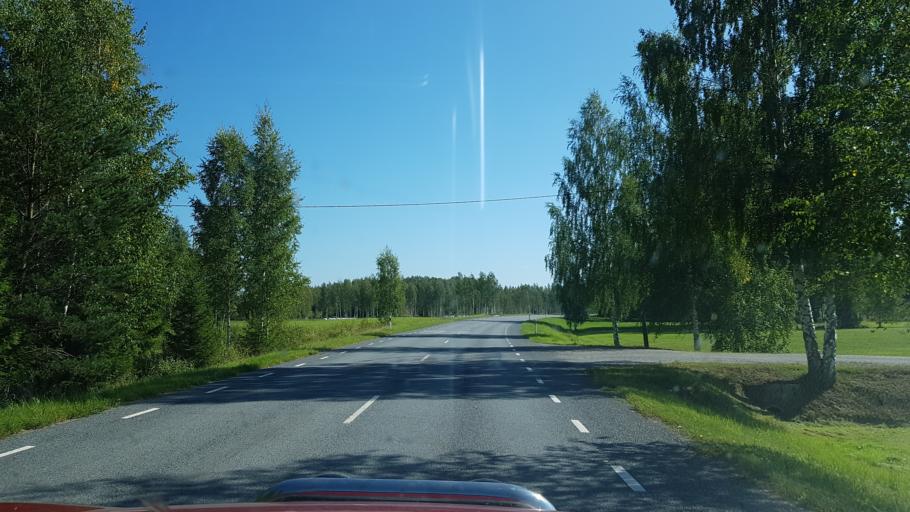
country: EE
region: Polvamaa
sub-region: Polva linn
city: Polva
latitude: 58.2773
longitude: 27.1051
